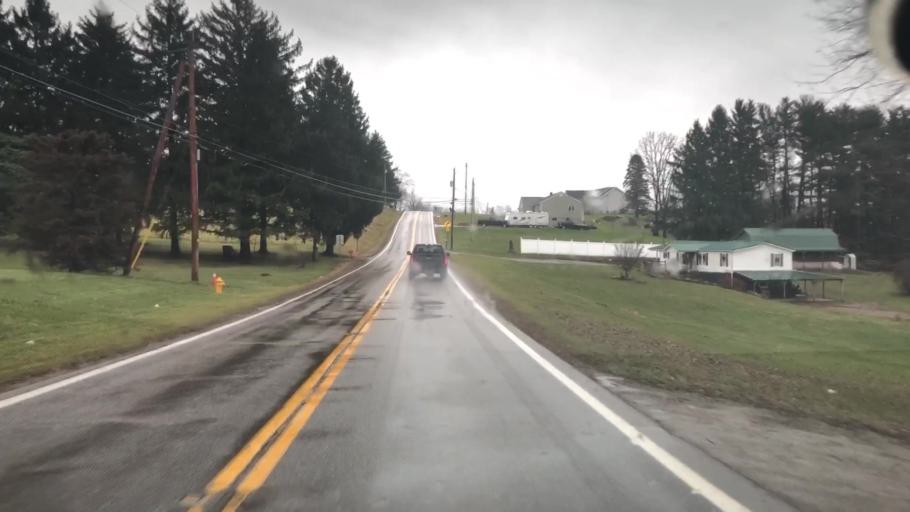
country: US
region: Ohio
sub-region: Belmont County
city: Saint Clairsville
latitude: 40.1062
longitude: -80.9270
